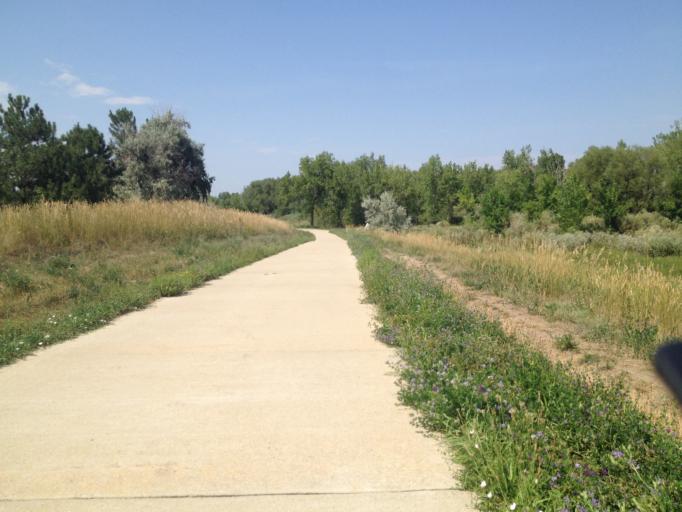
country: US
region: Colorado
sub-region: Boulder County
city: Boulder
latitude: 40.0210
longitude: -105.2162
